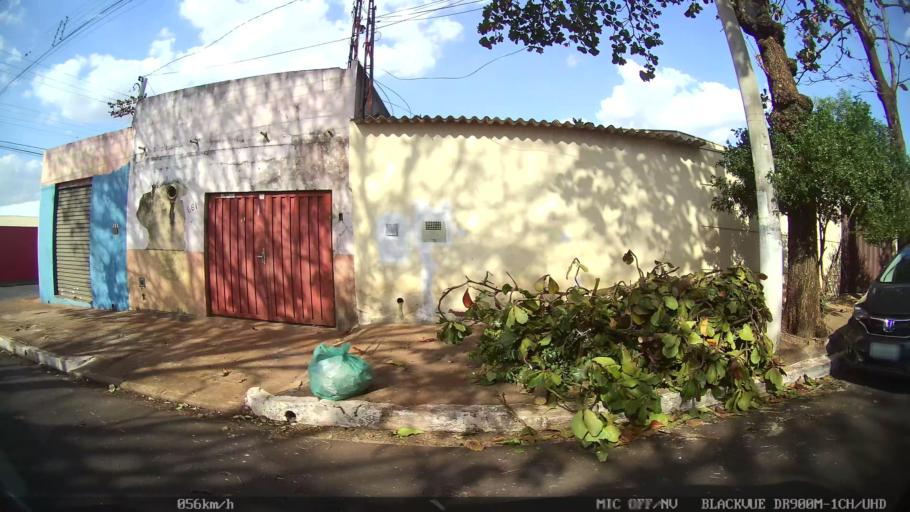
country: BR
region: Sao Paulo
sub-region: Ribeirao Preto
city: Ribeirao Preto
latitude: -21.1849
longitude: -47.8339
